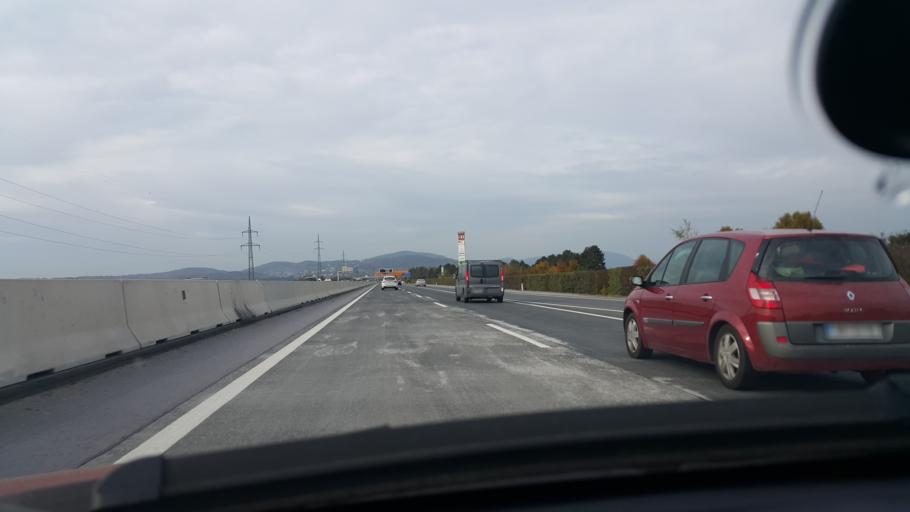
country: AT
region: Styria
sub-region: Politischer Bezirk Graz-Umgebung
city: Unterpremstatten
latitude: 46.9764
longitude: 15.4254
